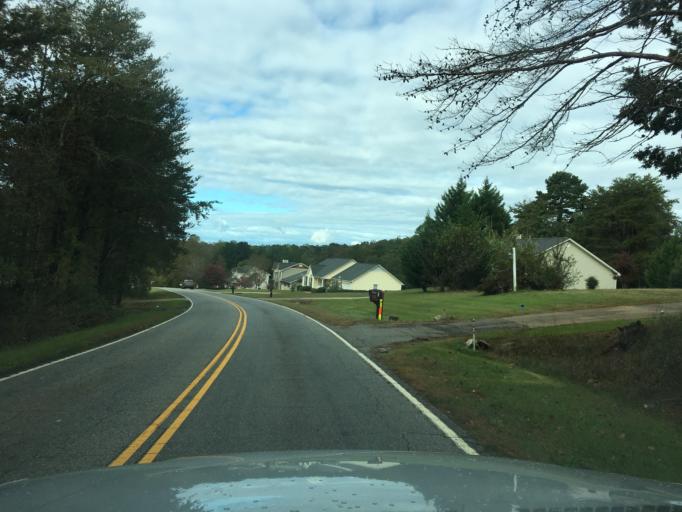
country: US
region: South Carolina
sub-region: Greenville County
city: Greer
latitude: 34.9782
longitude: -82.2118
